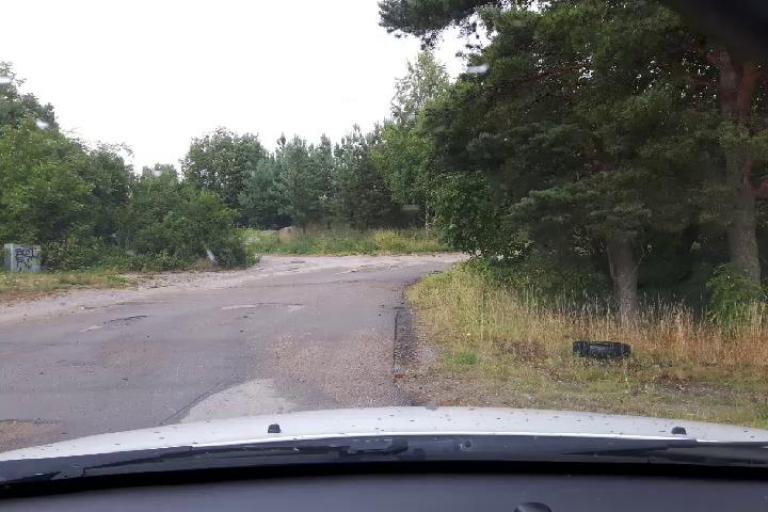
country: SE
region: Uppsala
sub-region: Uppsala Kommun
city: Gamla Uppsala
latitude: 59.8820
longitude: 17.6214
